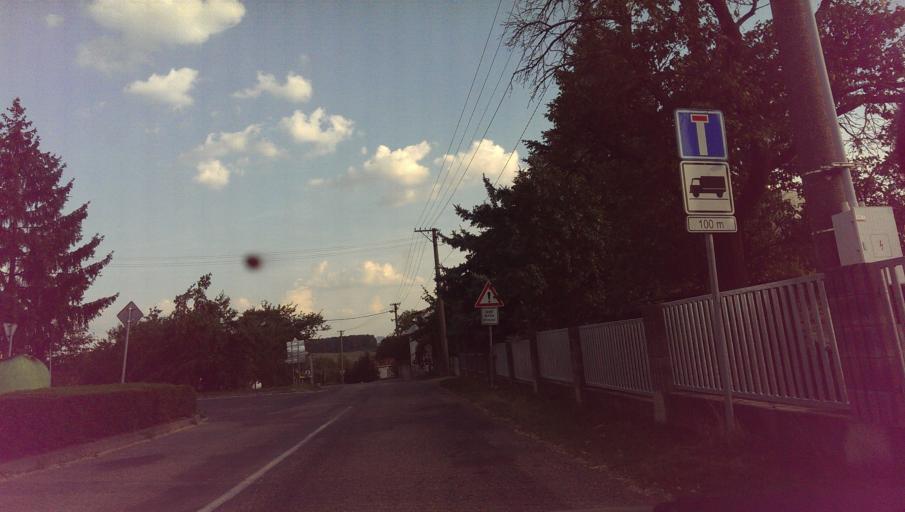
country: CZ
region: Zlin
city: Hvozdna
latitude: 49.2567
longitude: 17.7567
